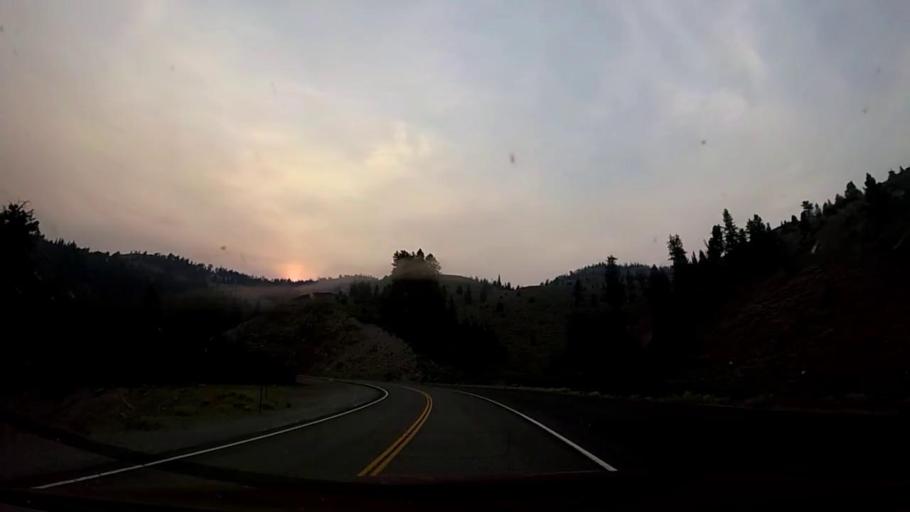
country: US
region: Idaho
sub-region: Blaine County
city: Ketchum
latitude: 43.8868
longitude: -114.6944
